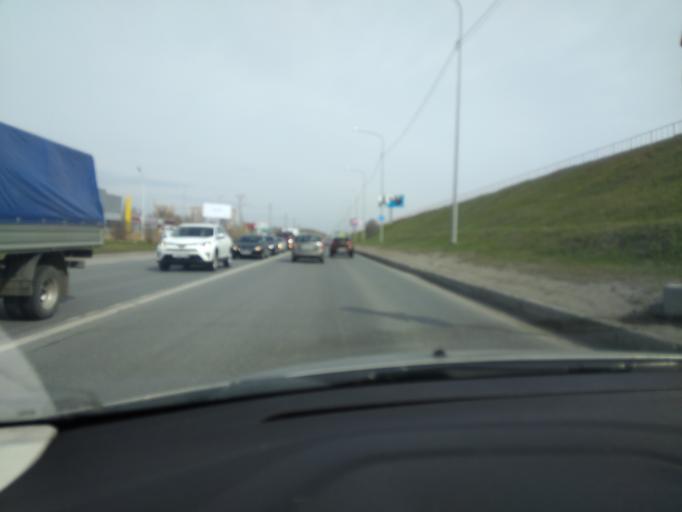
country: RU
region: Tjumen
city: Melioratorov
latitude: 57.1642
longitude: 65.6003
